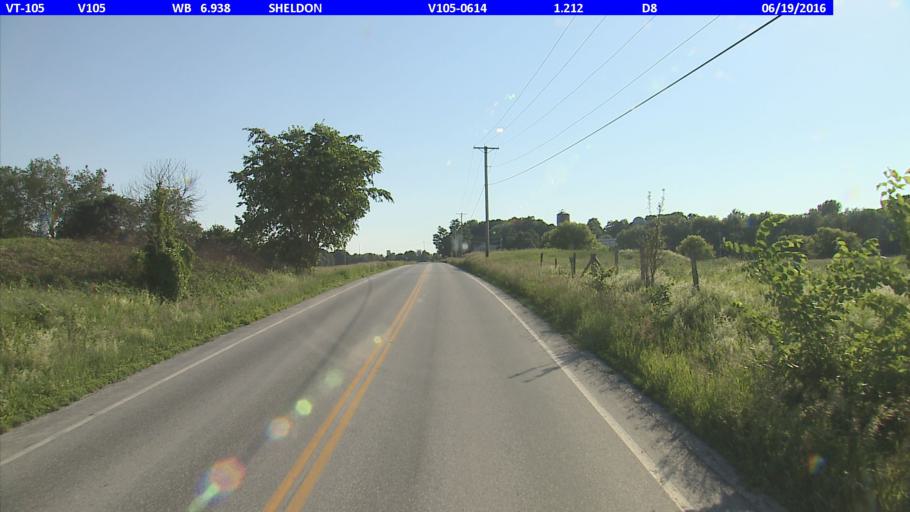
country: US
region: Vermont
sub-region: Franklin County
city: Saint Albans
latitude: 44.8983
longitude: -73.0053
